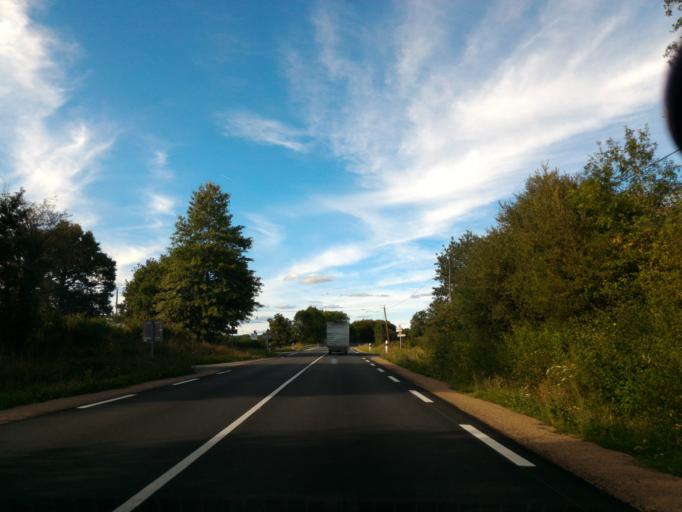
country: FR
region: Limousin
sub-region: Departement de la Haute-Vienne
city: Magnac-Laval
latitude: 46.1608
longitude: 1.1328
